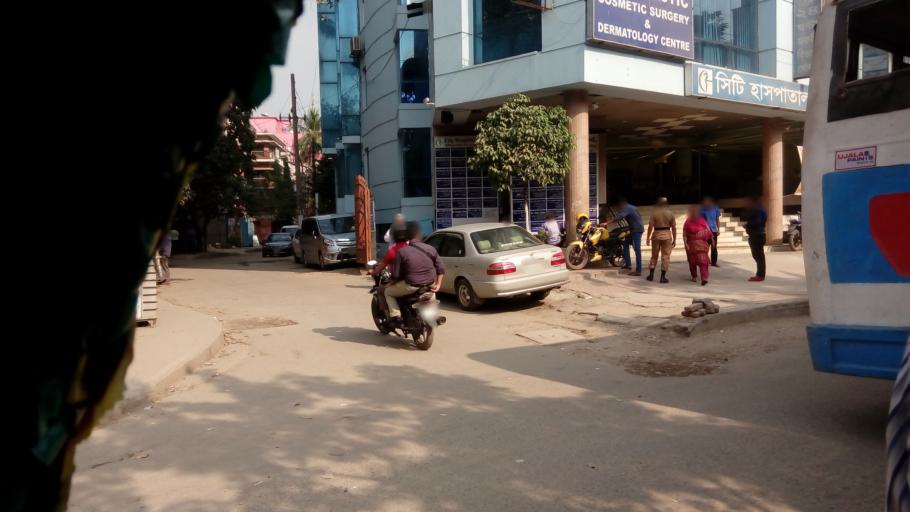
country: BD
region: Dhaka
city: Azimpur
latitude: 23.7541
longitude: 90.3651
